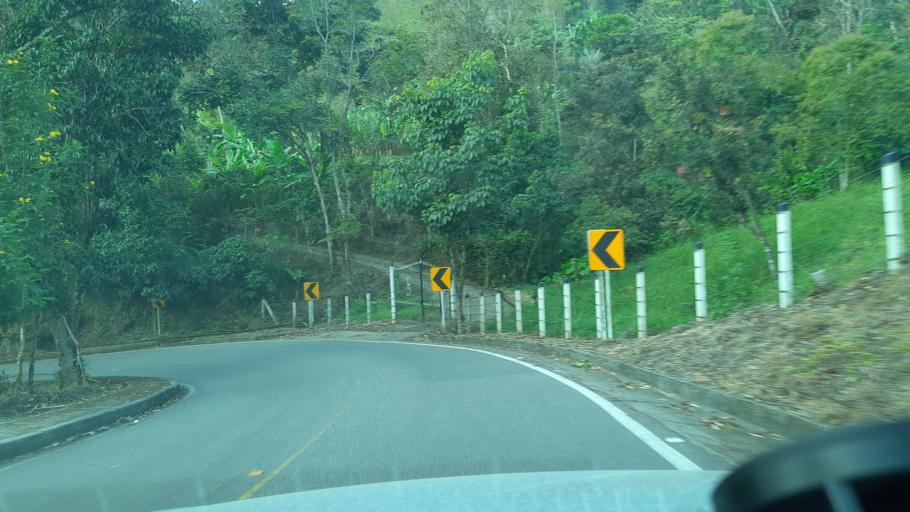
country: CO
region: Boyaca
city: Chivor
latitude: 4.9758
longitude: -73.3286
